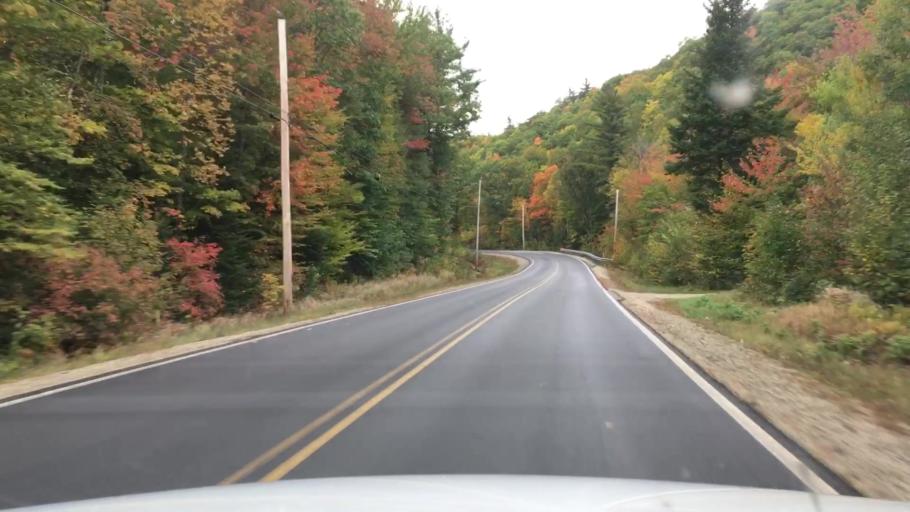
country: US
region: Maine
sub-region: Oxford County
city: Bethel
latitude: 44.2955
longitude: -70.7363
